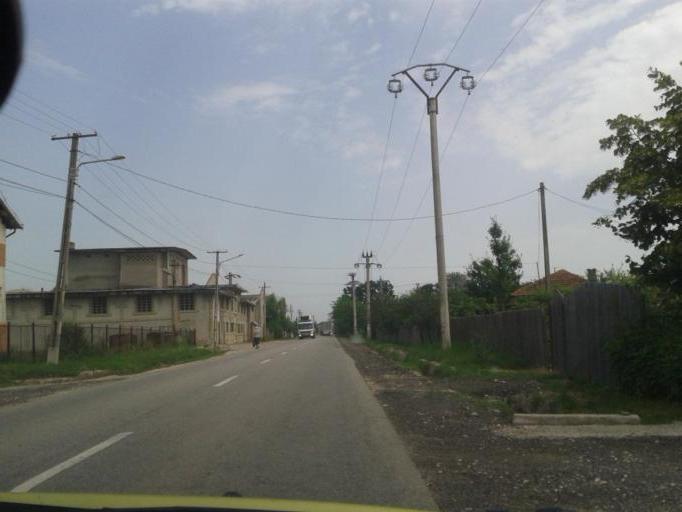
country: RO
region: Dambovita
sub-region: Comuna Petresti
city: Petresti
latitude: 44.6749
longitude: 25.3103
